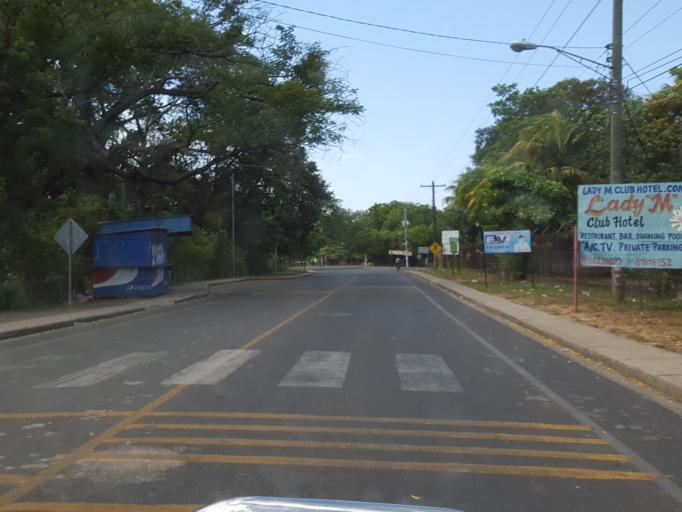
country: NI
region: Leon
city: Leon
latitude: 12.4346
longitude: -86.9013
